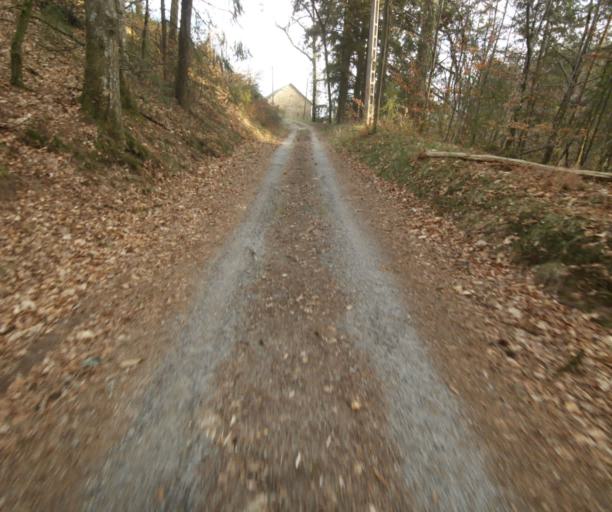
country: FR
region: Limousin
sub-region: Departement de la Correze
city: Correze
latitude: 45.3825
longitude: 1.8519
